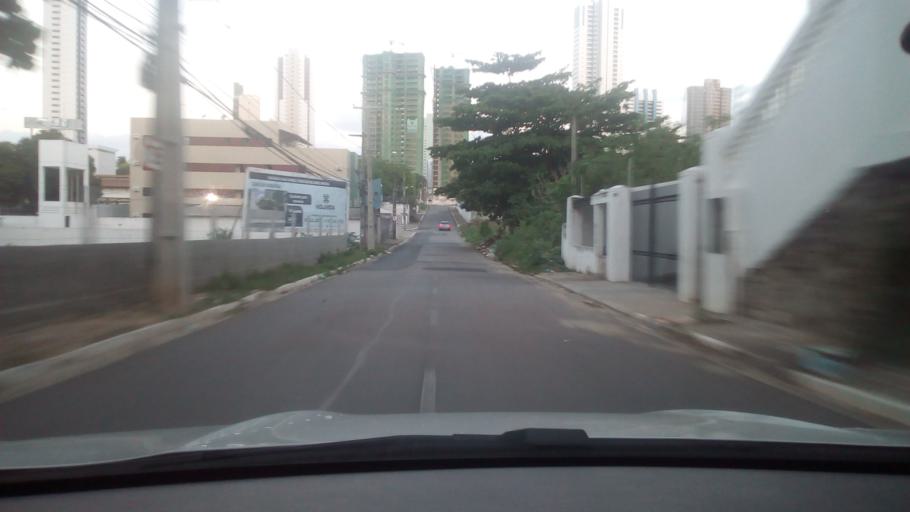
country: BR
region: Paraiba
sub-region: Joao Pessoa
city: Joao Pessoa
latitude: -7.1145
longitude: -34.8450
